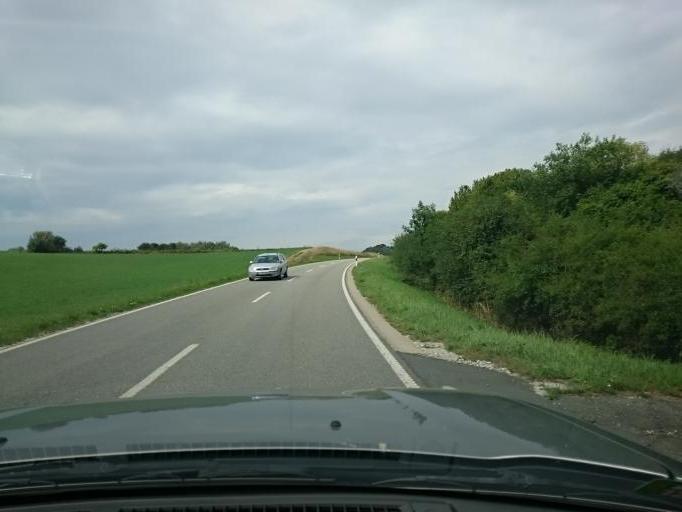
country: DE
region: Bavaria
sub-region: Regierungsbezirk Mittelfranken
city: Velden
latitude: 49.6471
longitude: 11.4772
